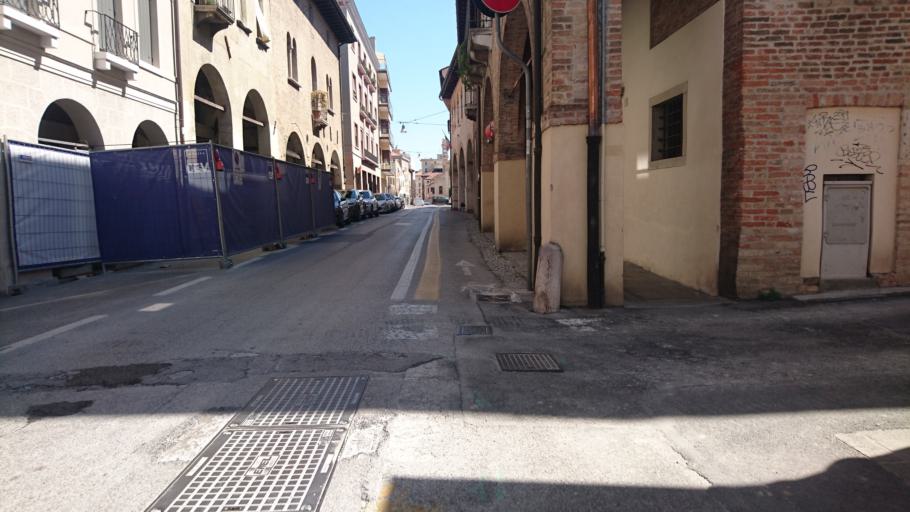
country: IT
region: Veneto
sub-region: Provincia di Treviso
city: Treviso
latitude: 45.6636
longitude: 12.2410
